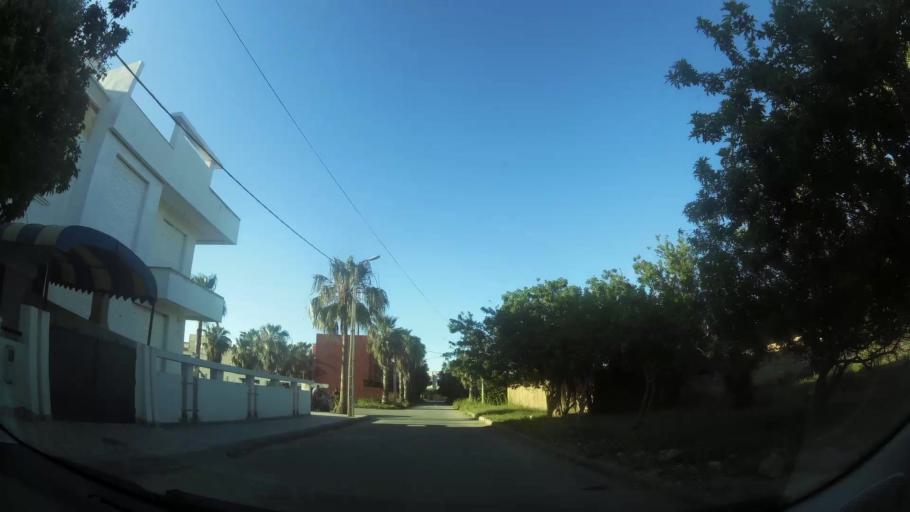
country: MA
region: Oriental
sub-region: Berkane-Taourirt
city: Madagh
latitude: 35.0824
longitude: -2.2460
